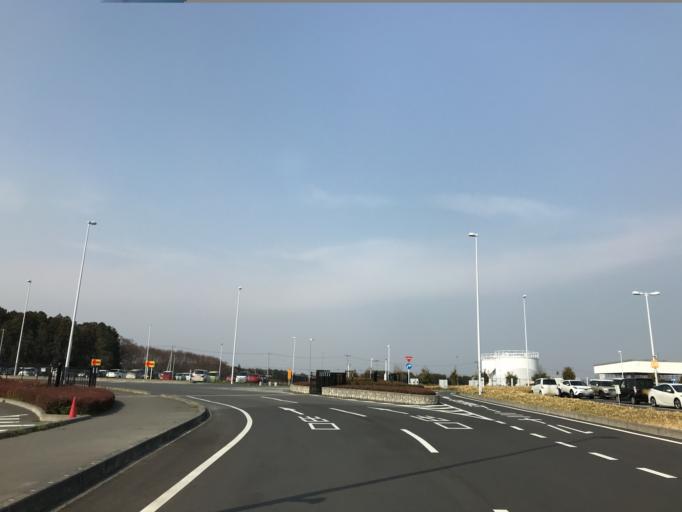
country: JP
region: Ibaraki
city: Okunoya
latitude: 36.1784
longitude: 140.4060
